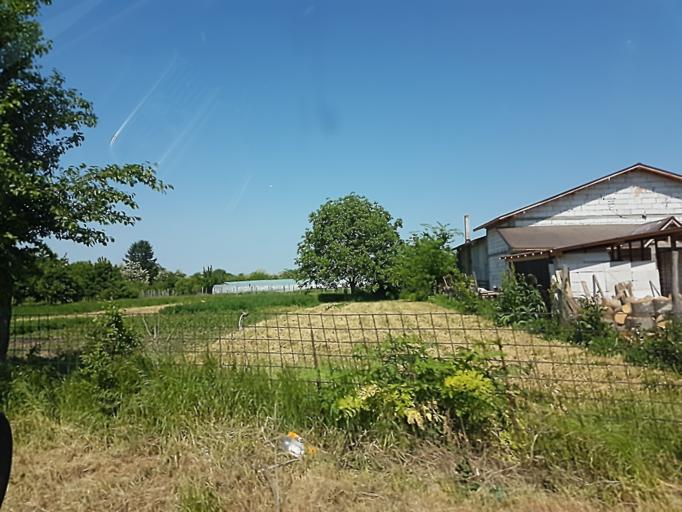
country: RO
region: Giurgiu
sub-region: Comuna Herasti
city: Herasti
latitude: 44.2157
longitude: 26.3587
